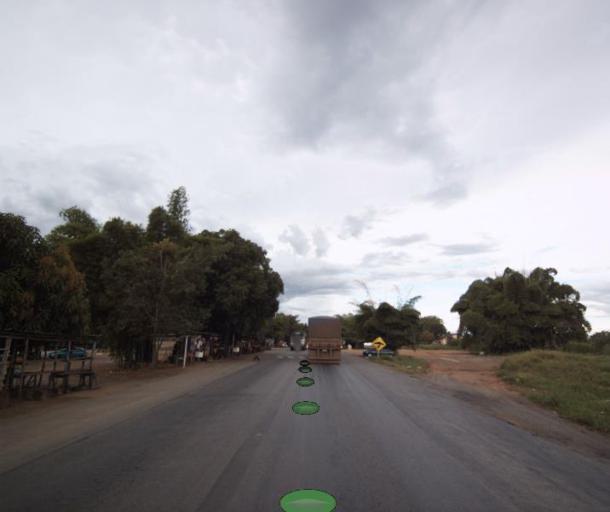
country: BR
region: Goias
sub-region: Itapaci
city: Itapaci
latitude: -15.0387
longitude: -49.4382
